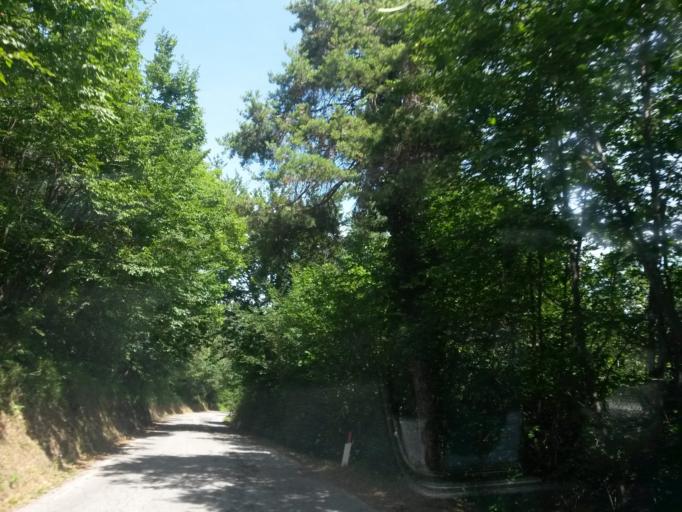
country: IT
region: Lombardy
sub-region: Provincia di Brescia
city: Gardola
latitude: 45.7685
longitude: 10.7171
